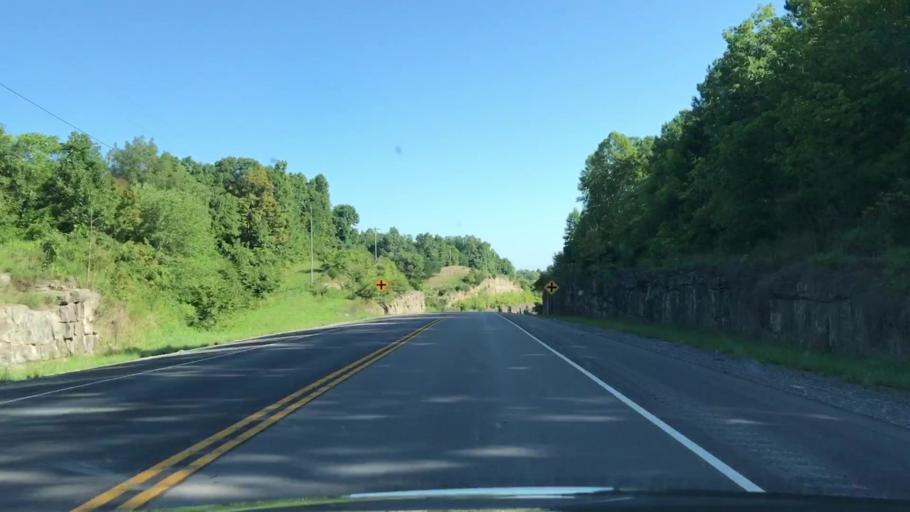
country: US
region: Kentucky
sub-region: Cumberland County
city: Burkesville
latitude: 36.7014
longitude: -85.3721
